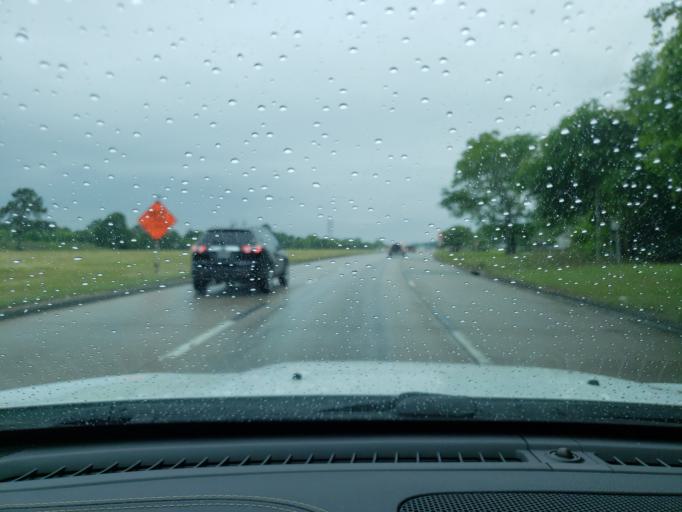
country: US
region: Texas
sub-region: Harris County
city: Baytown
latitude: 29.7575
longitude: -94.9307
